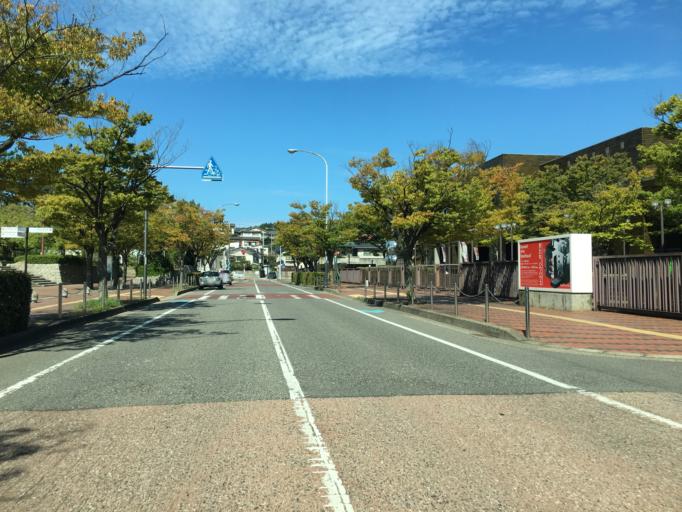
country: JP
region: Niigata
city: Niigata-shi
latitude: 37.9277
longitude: 139.0421
